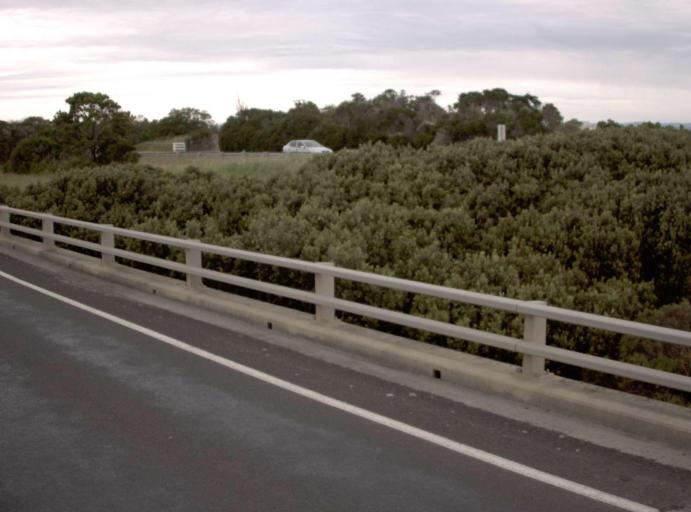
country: AU
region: Victoria
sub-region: Casey
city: Tooradin
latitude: -38.2118
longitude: 145.4270
